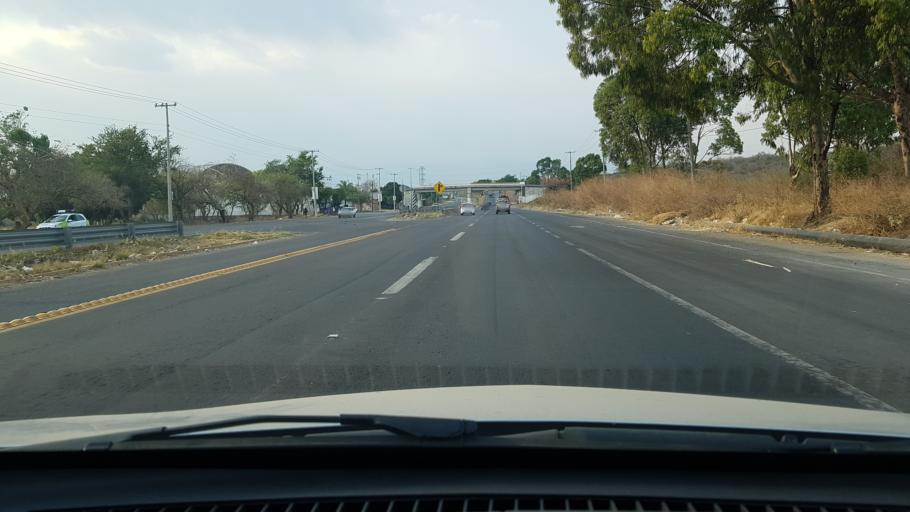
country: MX
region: Morelos
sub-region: Yecapixtla
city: Juan Morales
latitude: 18.8344
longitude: -98.9230
